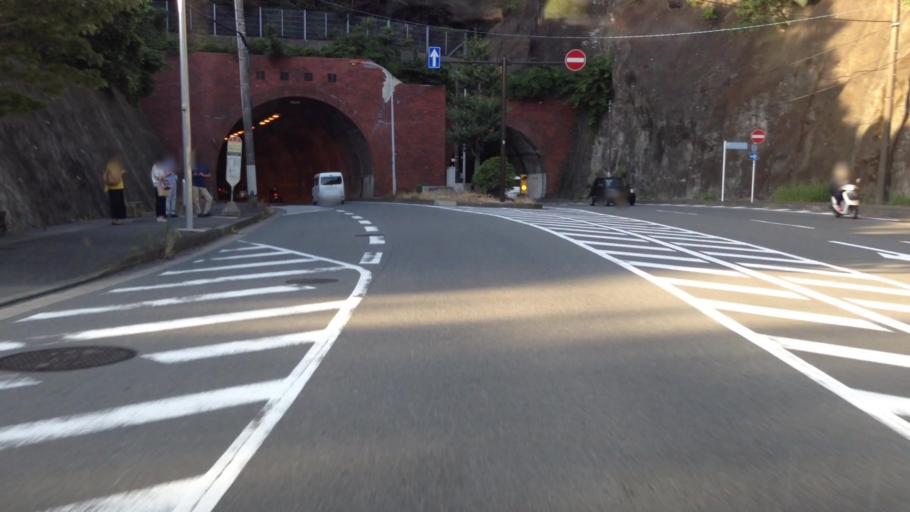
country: JP
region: Kanagawa
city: Yokosuka
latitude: 35.2332
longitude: 139.6579
